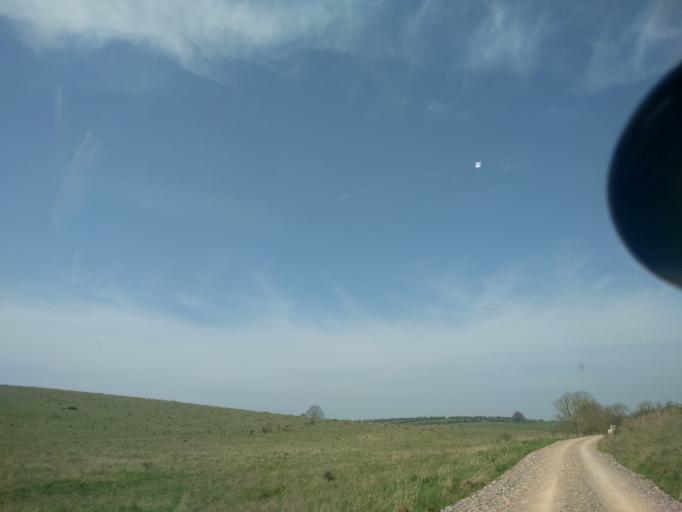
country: GB
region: England
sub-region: Wiltshire
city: Edington
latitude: 51.2428
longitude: -2.0979
